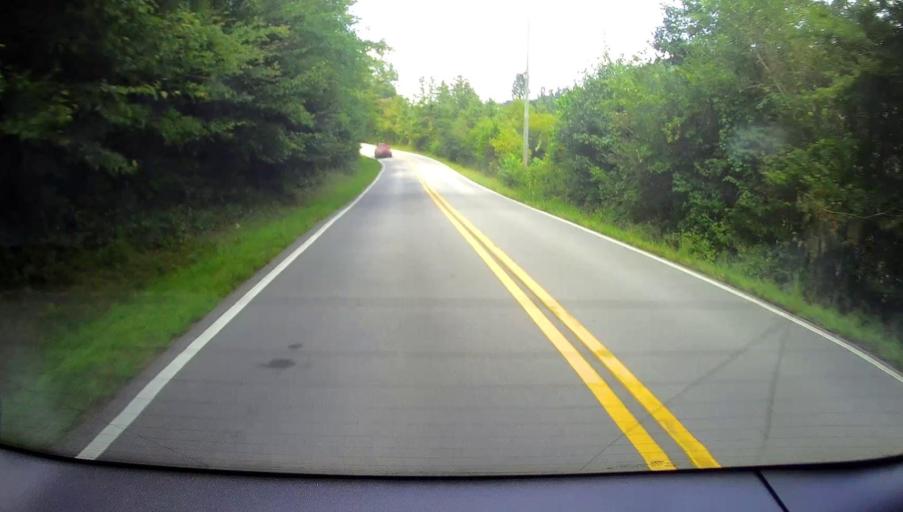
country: US
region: Georgia
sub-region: Catoosa County
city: Ringgold
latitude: 34.9473
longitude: -85.0800
